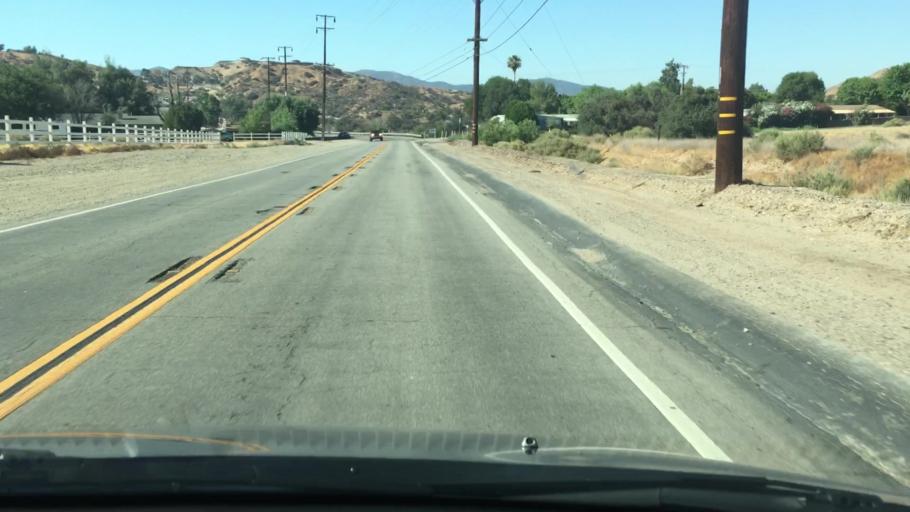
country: US
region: California
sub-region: Los Angeles County
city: Agua Dulce
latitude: 34.4576
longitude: -118.4214
